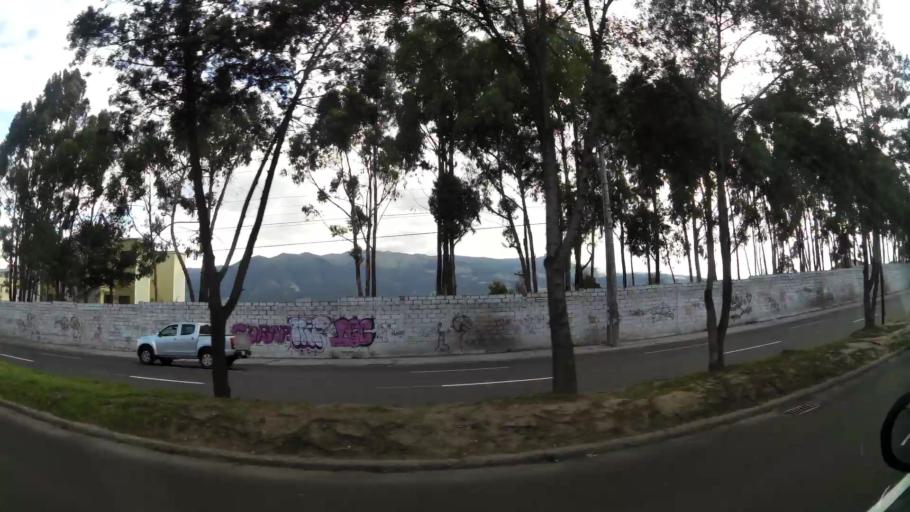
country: EC
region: Pichincha
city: Quito
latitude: -0.1351
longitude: -78.4732
